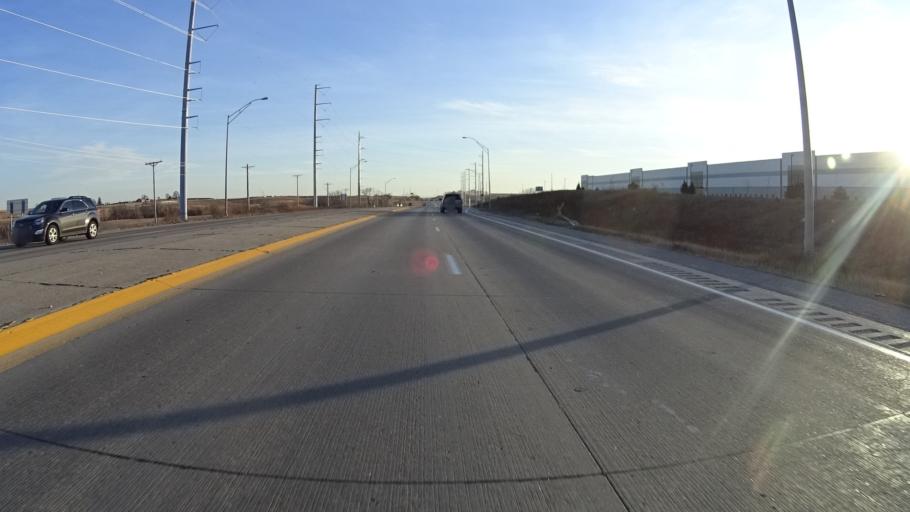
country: US
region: Nebraska
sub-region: Sarpy County
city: Chalco
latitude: 41.1440
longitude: -96.1390
